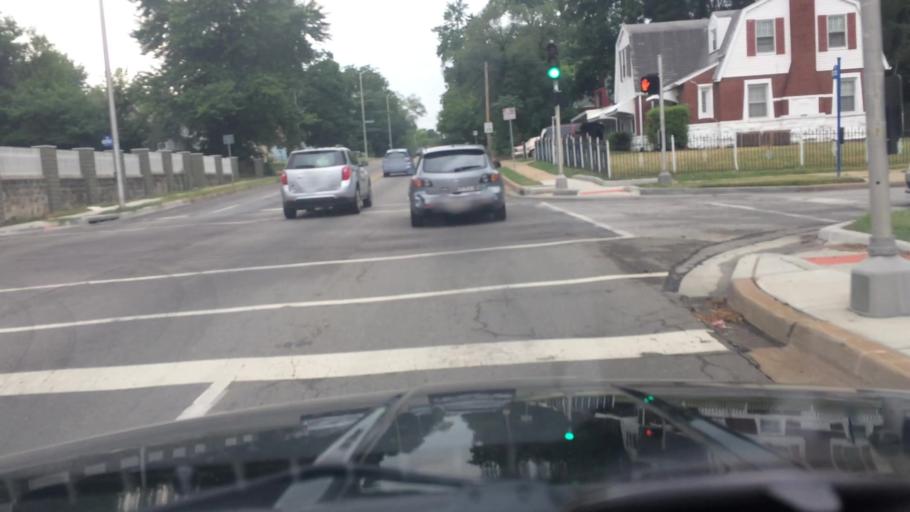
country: US
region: Kansas
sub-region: Johnson County
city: Leawood
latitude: 38.9913
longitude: -94.5663
